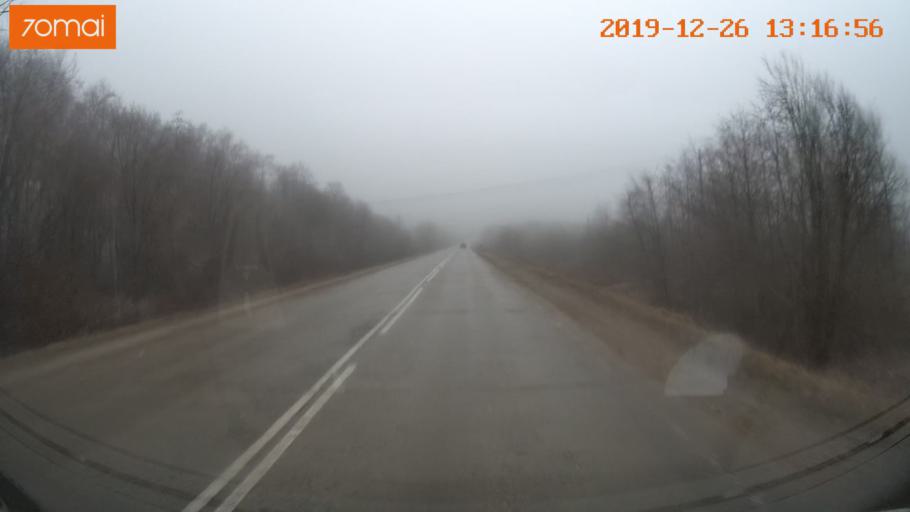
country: RU
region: Vologda
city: Cherepovets
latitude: 58.9758
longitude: 38.1106
